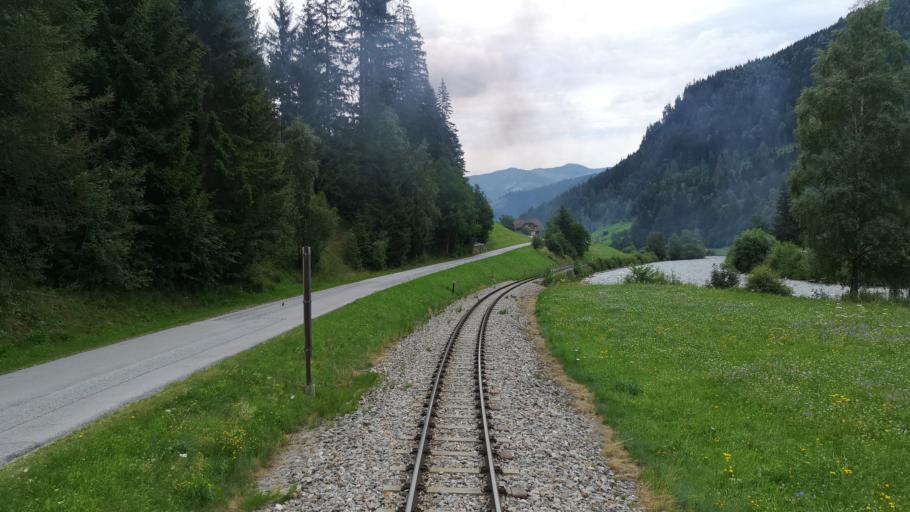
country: AT
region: Salzburg
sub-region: Politischer Bezirk Tamsweg
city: Ramingstein
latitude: 47.0764
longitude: 13.8496
